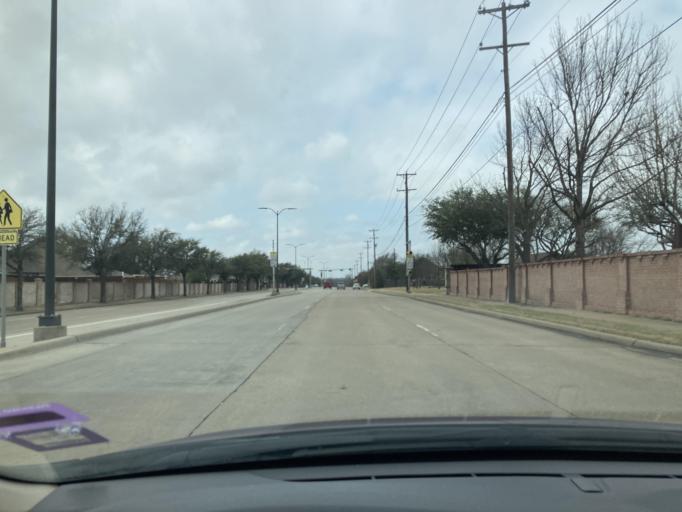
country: US
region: Texas
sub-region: Collin County
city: Parker
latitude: 33.0858
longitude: -96.6344
